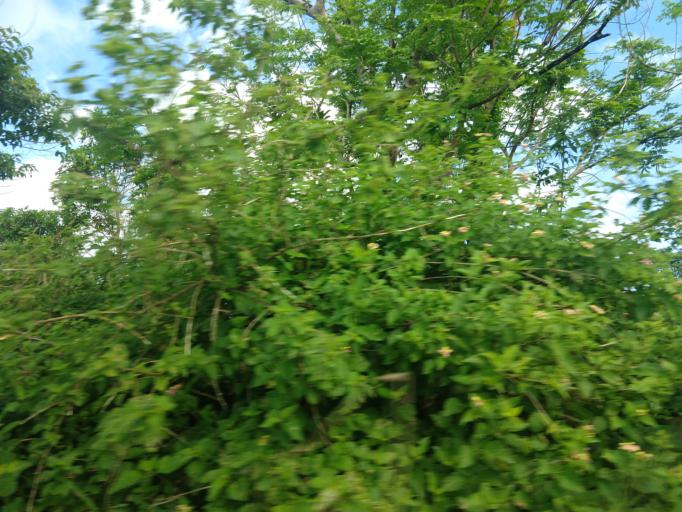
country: MZ
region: Sofala
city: Beira
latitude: -19.6100
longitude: 35.1495
